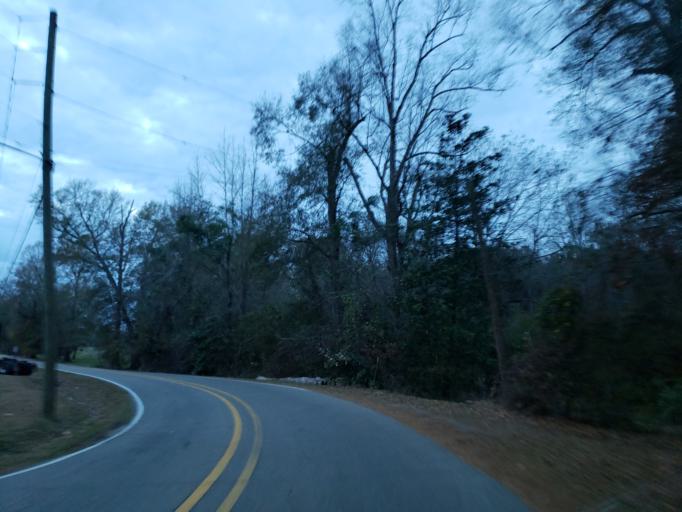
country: US
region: Mississippi
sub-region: Forrest County
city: Petal
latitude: 31.3356
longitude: -89.2586
